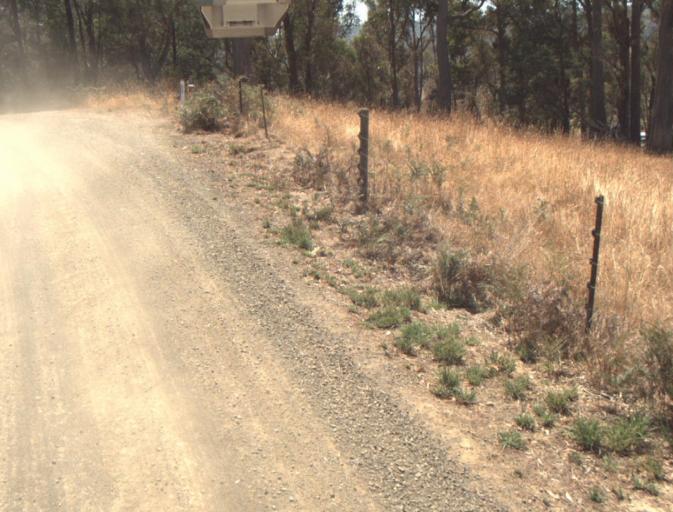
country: AU
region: Tasmania
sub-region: Launceston
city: Mayfield
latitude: -41.2477
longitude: 147.1348
